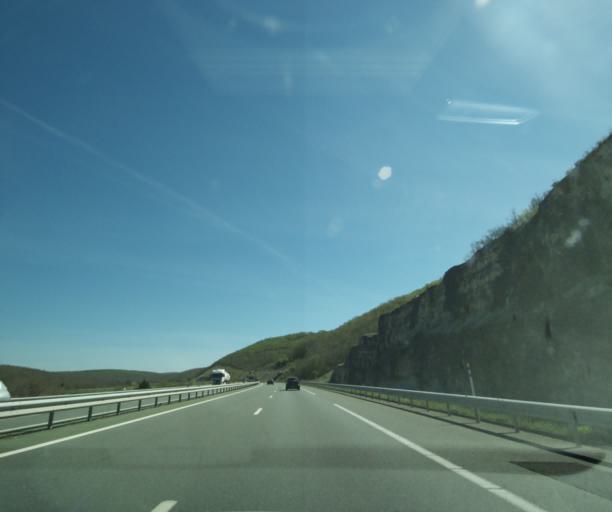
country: FR
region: Midi-Pyrenees
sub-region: Departement du Lot
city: Le Vigan
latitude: 44.8019
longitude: 1.5075
